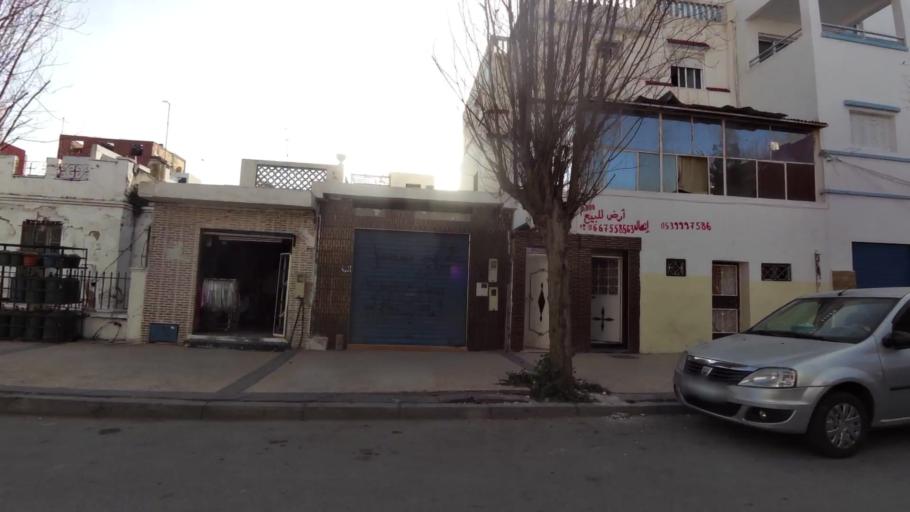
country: MA
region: Tanger-Tetouan
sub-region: Tetouan
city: Martil
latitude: 35.6181
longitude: -5.2770
